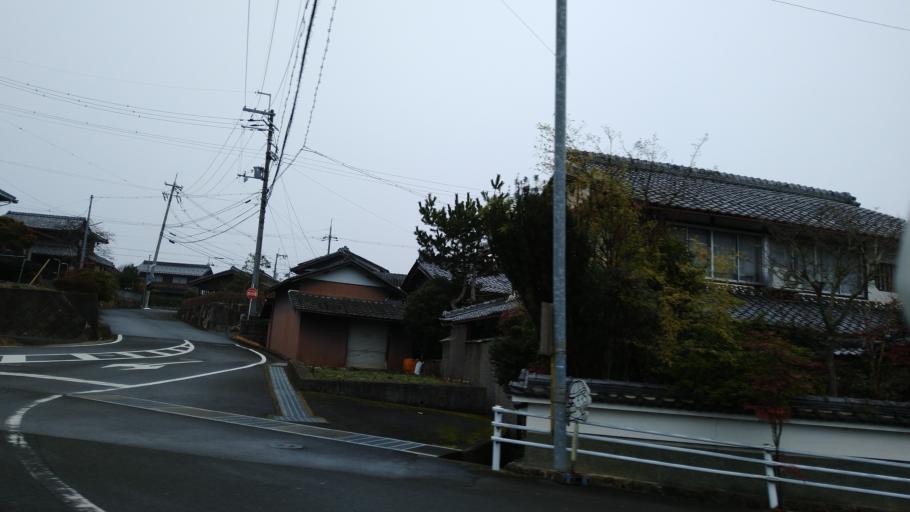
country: JP
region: Kyoto
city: Ayabe
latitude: 35.1657
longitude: 135.3967
